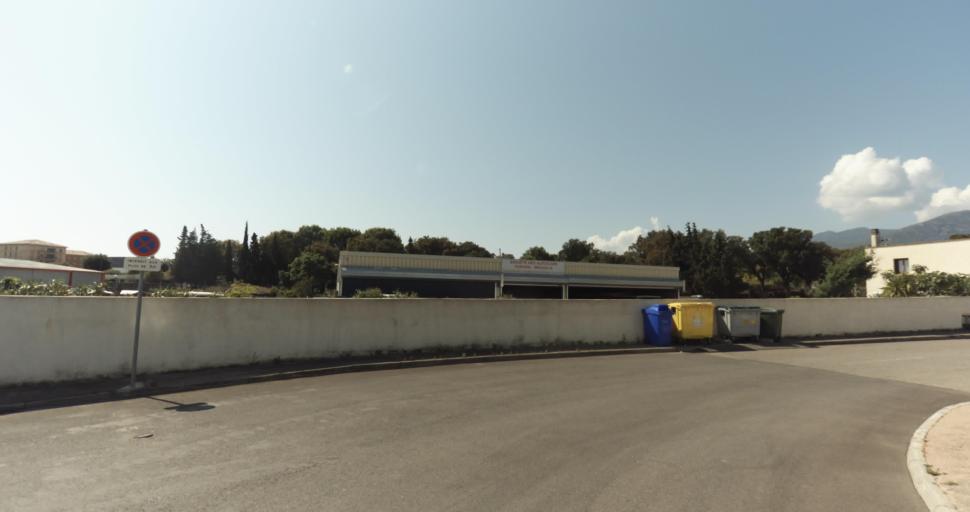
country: FR
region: Corsica
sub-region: Departement de la Haute-Corse
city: Biguglia
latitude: 42.6279
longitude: 9.4350
